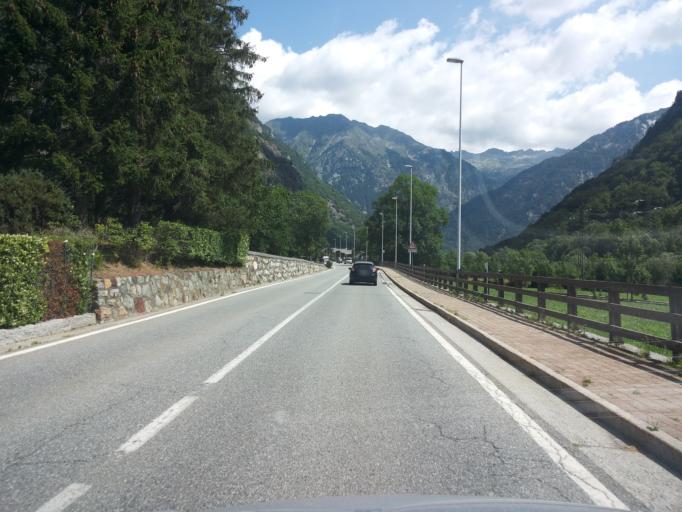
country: IT
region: Aosta Valley
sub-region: Valle d'Aosta
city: Issime
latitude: 45.6886
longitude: 7.8546
